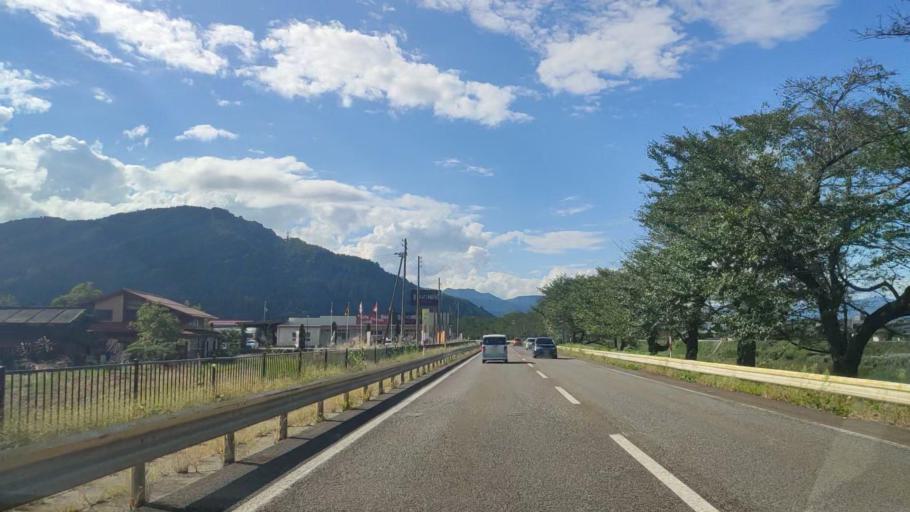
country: JP
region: Gifu
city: Takayama
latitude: 36.2078
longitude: 137.2169
